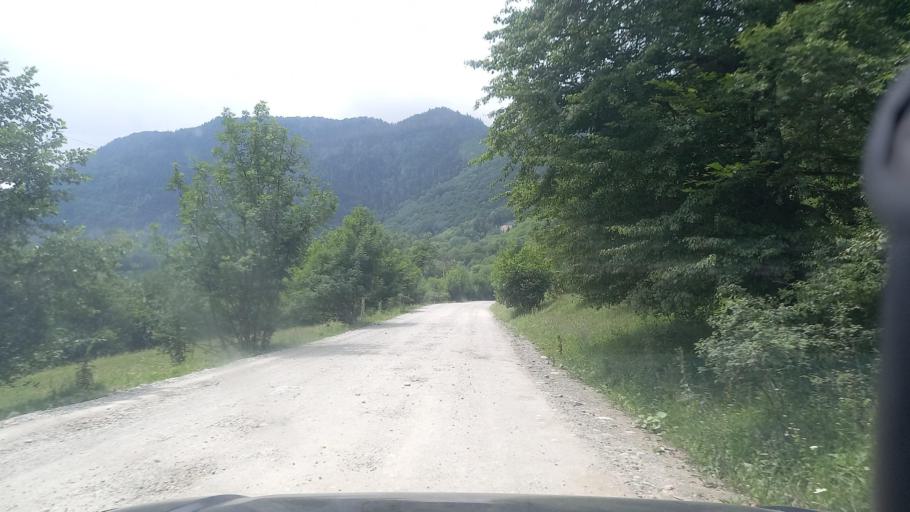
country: RU
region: Karachayevo-Cherkesiya
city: Kurdzhinovo
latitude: 43.9057
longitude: 40.9516
